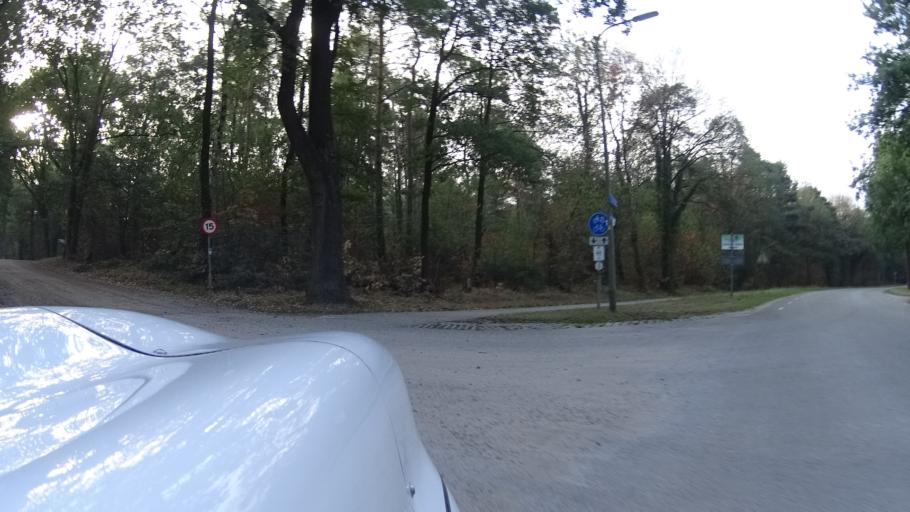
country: NL
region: Limburg
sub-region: Gemeente Venlo
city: Arcen
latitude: 51.4887
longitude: 6.2081
